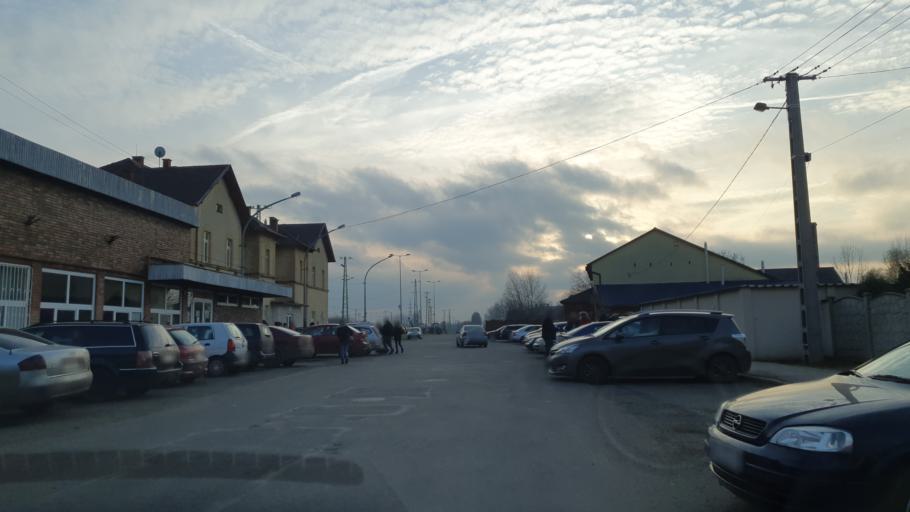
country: HU
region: Szabolcs-Szatmar-Bereg
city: Kisvarda
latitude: 48.2089
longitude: 22.0783
